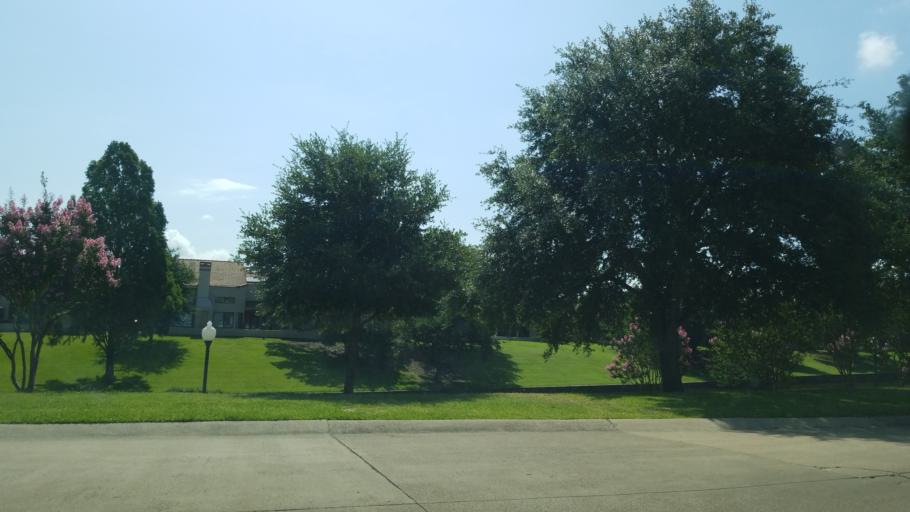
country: US
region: Texas
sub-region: Dallas County
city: Farmers Branch
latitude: 32.9299
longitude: -96.9544
